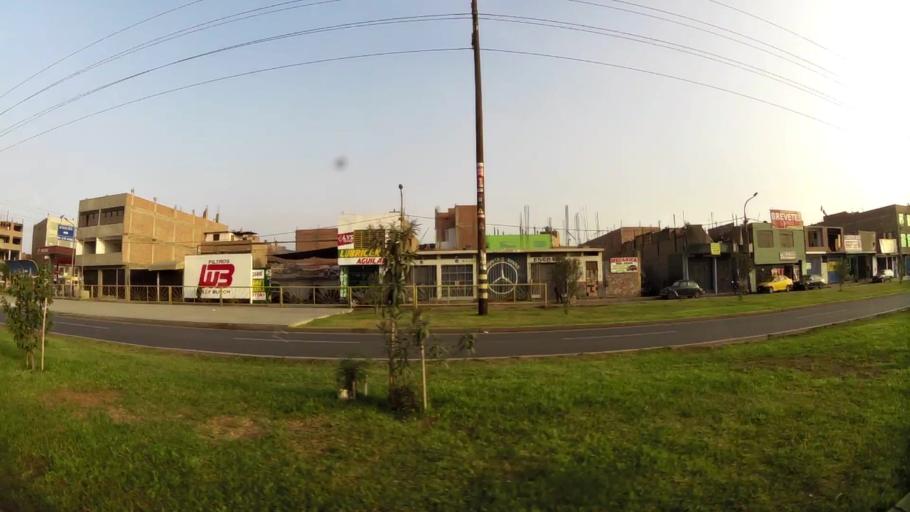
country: PE
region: Lima
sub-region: Lima
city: Independencia
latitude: -11.9898
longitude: -77.0980
